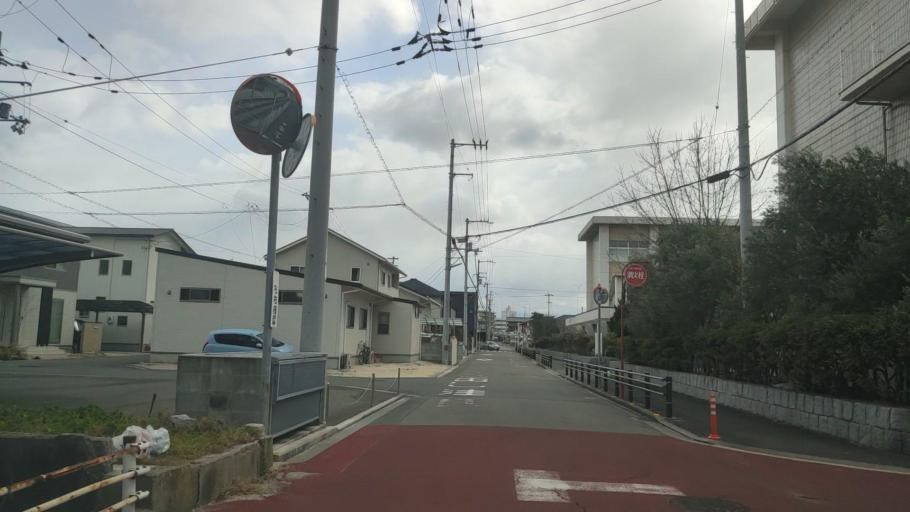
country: JP
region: Ehime
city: Saijo
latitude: 34.0607
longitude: 133.0133
